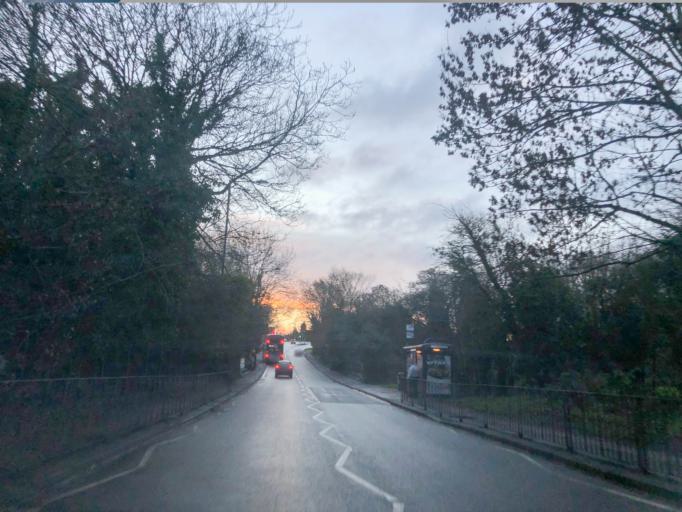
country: GB
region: England
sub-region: Solihull
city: Tidbury Green
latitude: 52.4154
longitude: -1.8879
